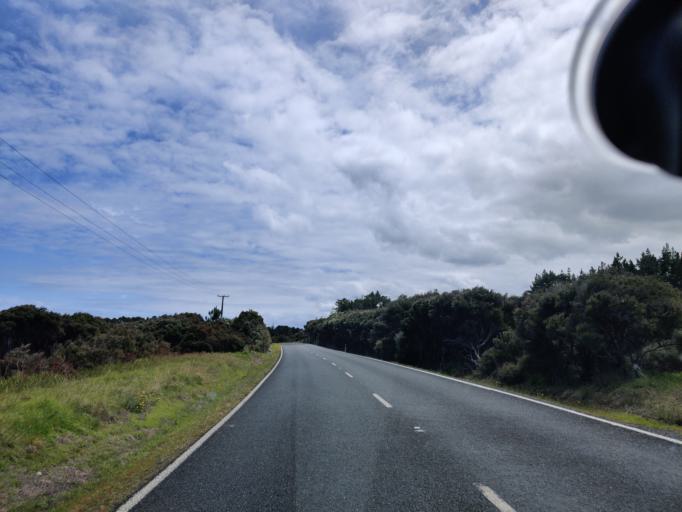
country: NZ
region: Northland
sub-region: Far North District
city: Kaitaia
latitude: -34.6656
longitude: 172.9734
